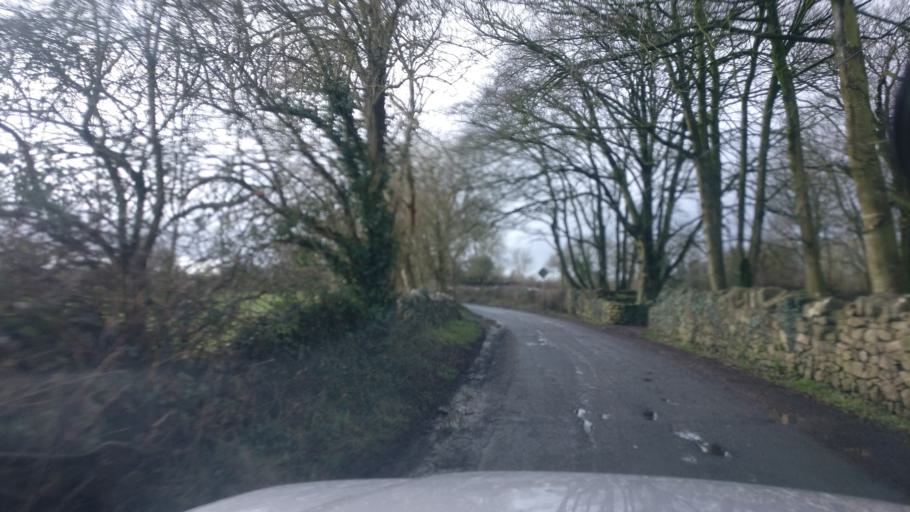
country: IE
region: Connaught
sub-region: County Galway
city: Athenry
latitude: 53.2655
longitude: -8.7921
